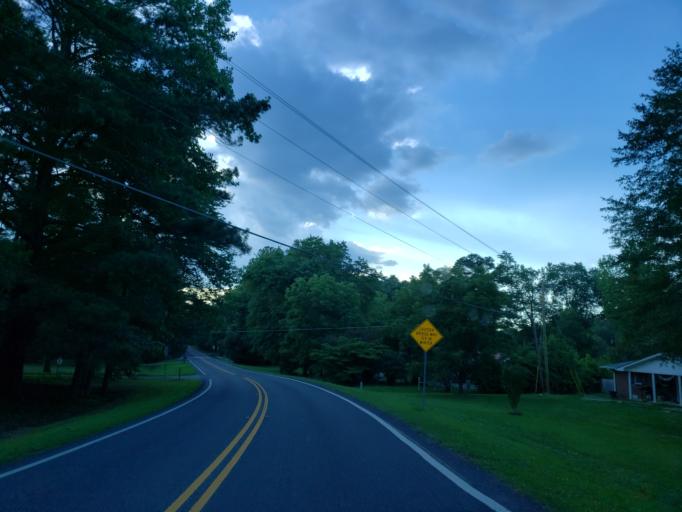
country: US
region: Georgia
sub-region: Bartow County
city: Emerson
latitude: 34.1974
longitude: -84.7368
